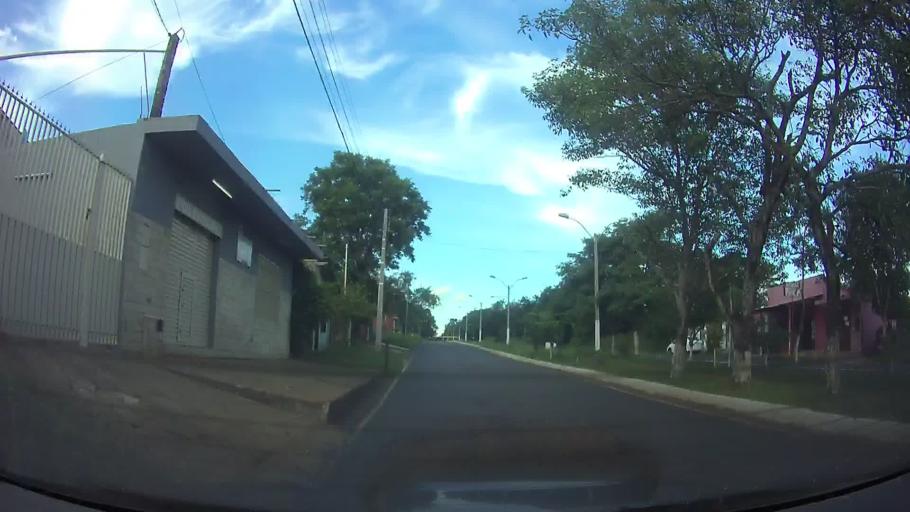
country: PY
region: Central
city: San Antonio
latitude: -25.4299
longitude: -57.5483
